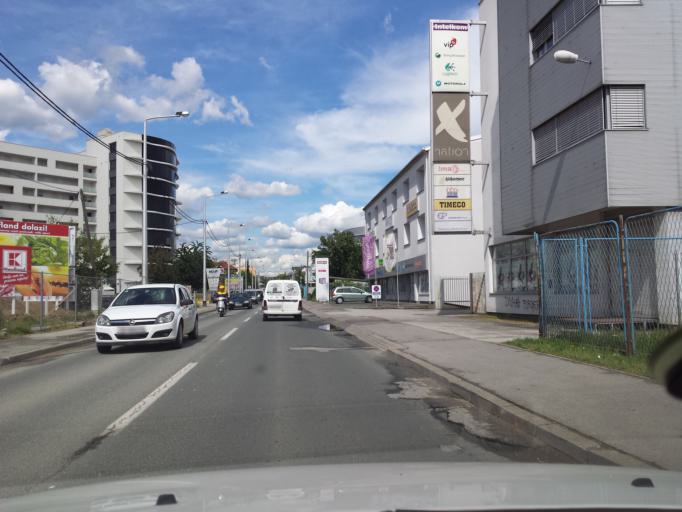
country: HR
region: Grad Zagreb
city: Jankomir
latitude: 45.8047
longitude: 15.9213
